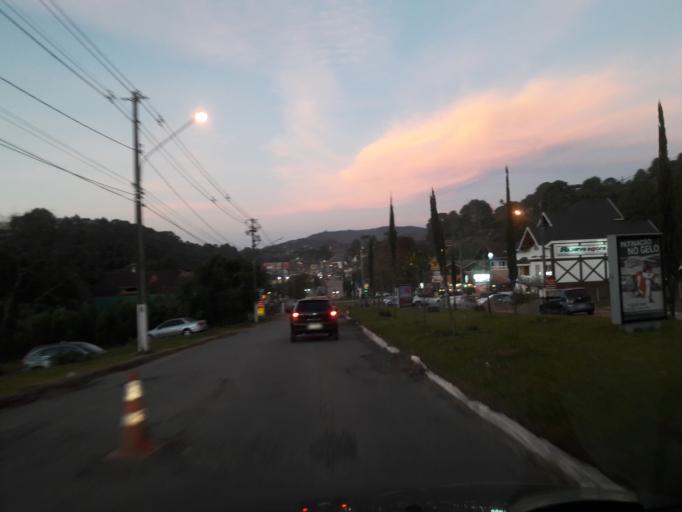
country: BR
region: Minas Gerais
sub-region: Camanducaia
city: Camanducaia
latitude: -22.8648
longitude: -46.0451
